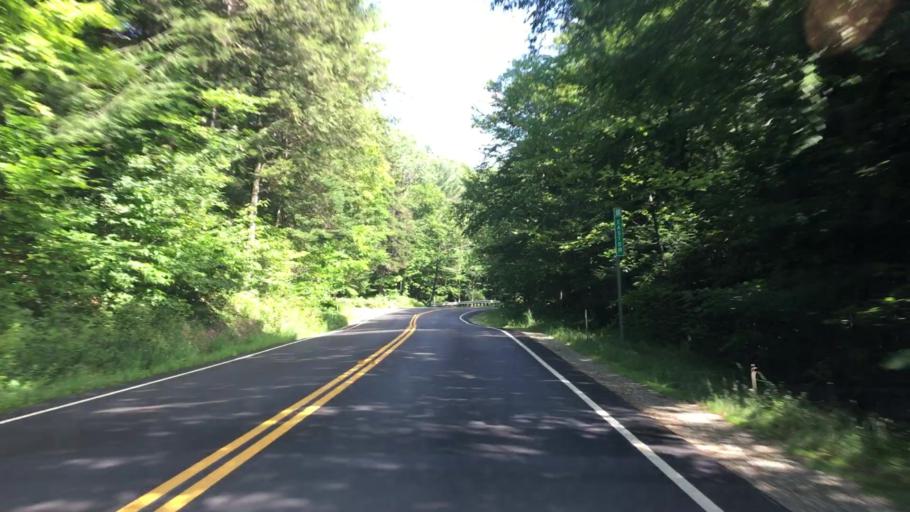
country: US
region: New Hampshire
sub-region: Grafton County
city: North Haverhill
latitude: 44.1010
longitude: -71.8541
